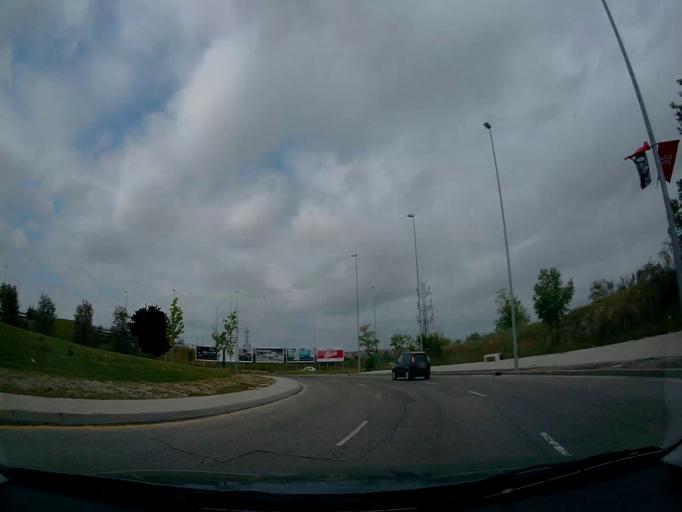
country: ES
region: Madrid
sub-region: Provincia de Madrid
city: Alcorcon
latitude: 40.3274
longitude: -3.8403
